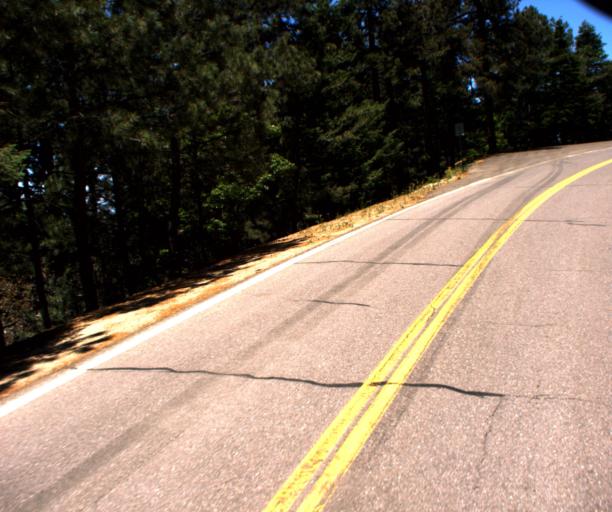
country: US
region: Arizona
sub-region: Graham County
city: Swift Trail Junction
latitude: 32.6287
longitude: -109.8391
